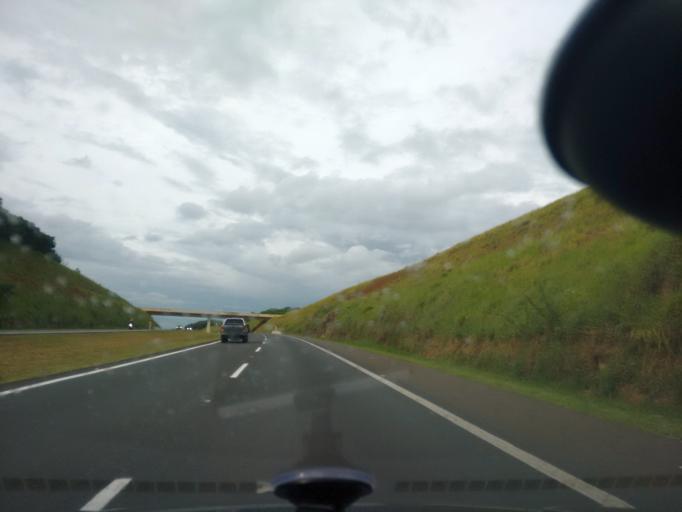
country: BR
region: Sao Paulo
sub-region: Cordeiropolis
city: Cordeiropolis
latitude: -22.5378
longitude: -47.4514
